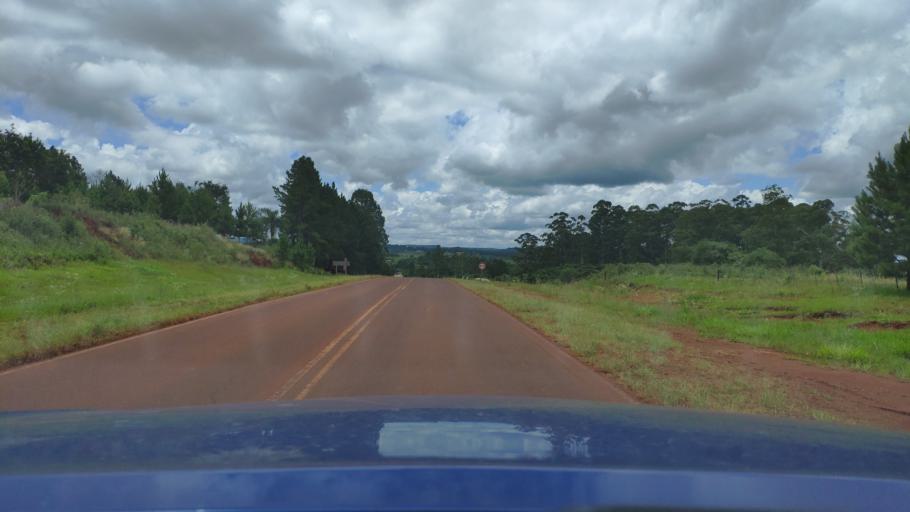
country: AR
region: Misiones
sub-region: Departamento de San Javier
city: San Javier
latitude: -27.8549
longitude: -55.2500
